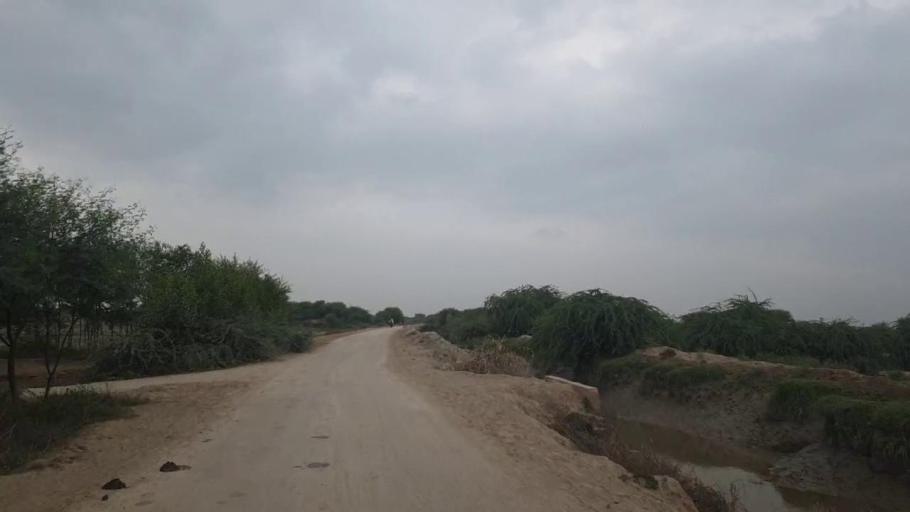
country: PK
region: Sindh
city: Badin
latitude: 24.6440
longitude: 68.6810
